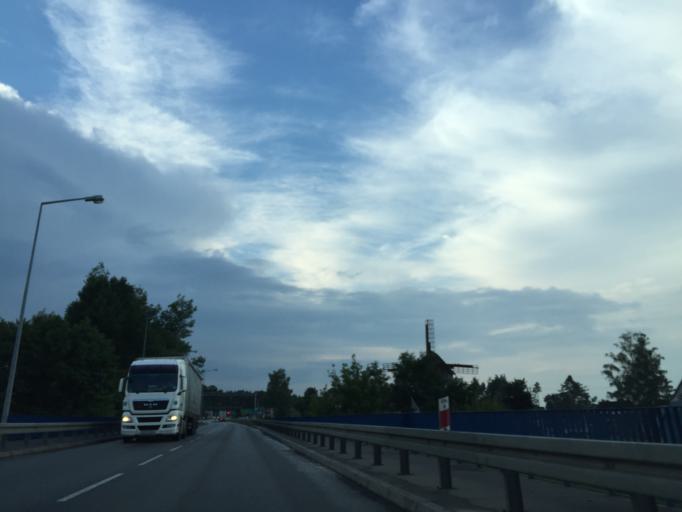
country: PL
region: Masovian Voivodeship
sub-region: Powiat ostrowski
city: Brok
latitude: 52.6952
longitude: 21.8490
